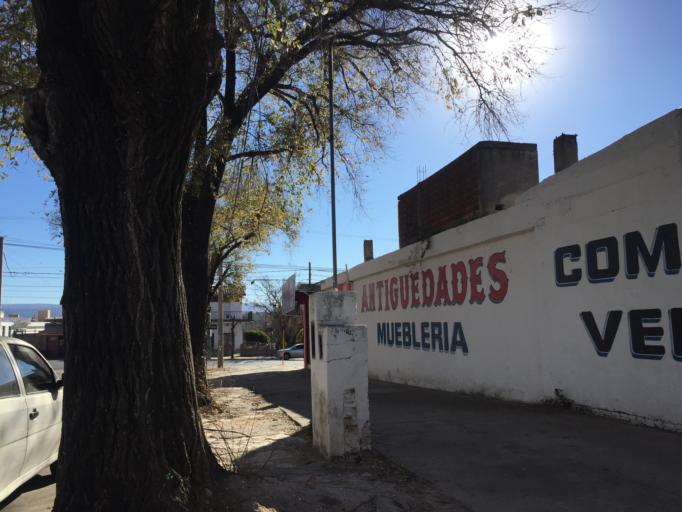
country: AR
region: Cordoba
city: Villa Carlos Paz
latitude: -31.4277
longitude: -64.4954
